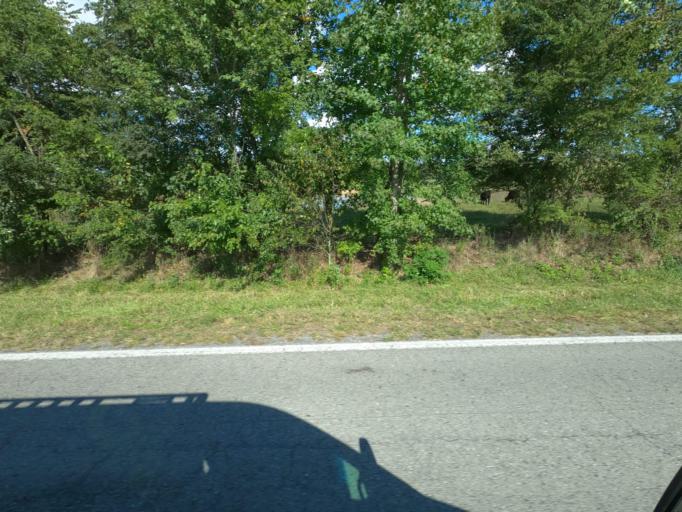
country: US
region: Illinois
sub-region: Massac County
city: Metropolis
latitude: 37.2584
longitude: -88.7518
